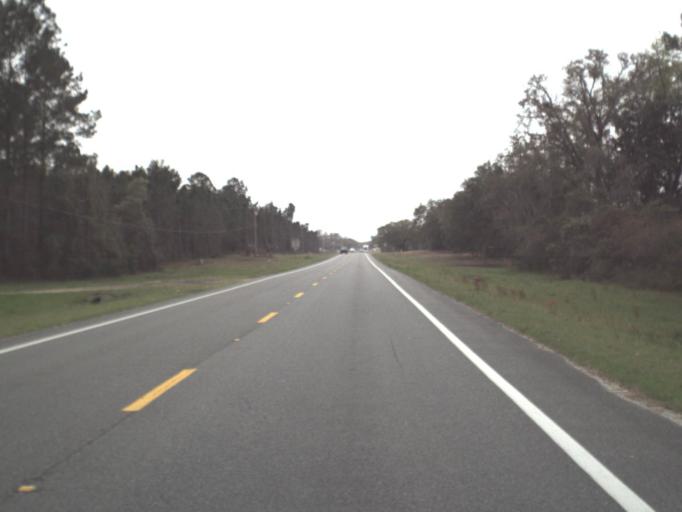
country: US
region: Florida
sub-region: Wakulla County
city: Crawfordville
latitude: 30.1138
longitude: -84.3744
